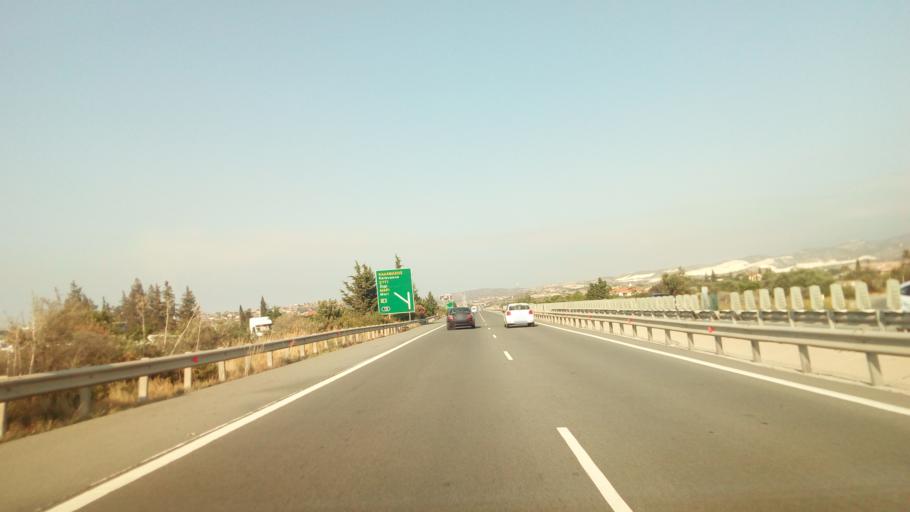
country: CY
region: Larnaka
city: Kofinou
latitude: 34.7553
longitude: 33.3178
